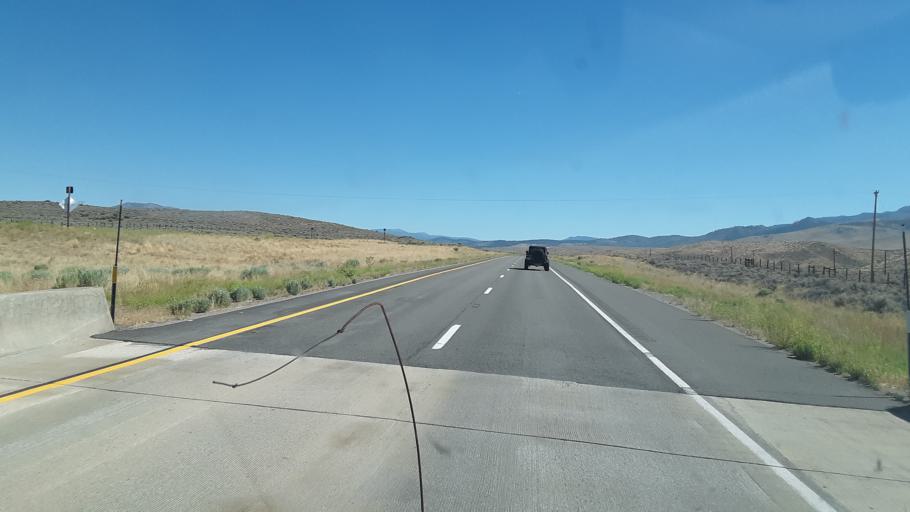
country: US
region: Nevada
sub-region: Washoe County
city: Cold Springs
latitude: 39.7242
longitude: -120.0386
